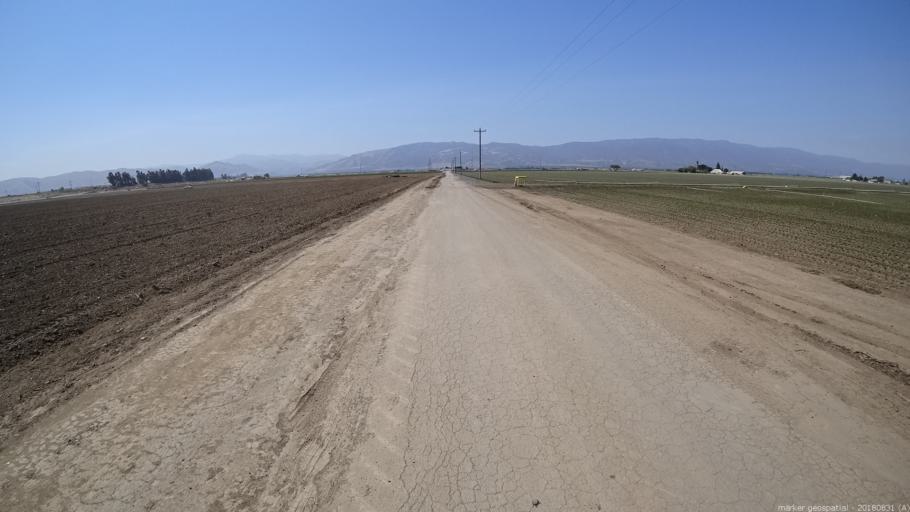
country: US
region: California
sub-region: Monterey County
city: Greenfield
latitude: 36.3534
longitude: -121.2637
